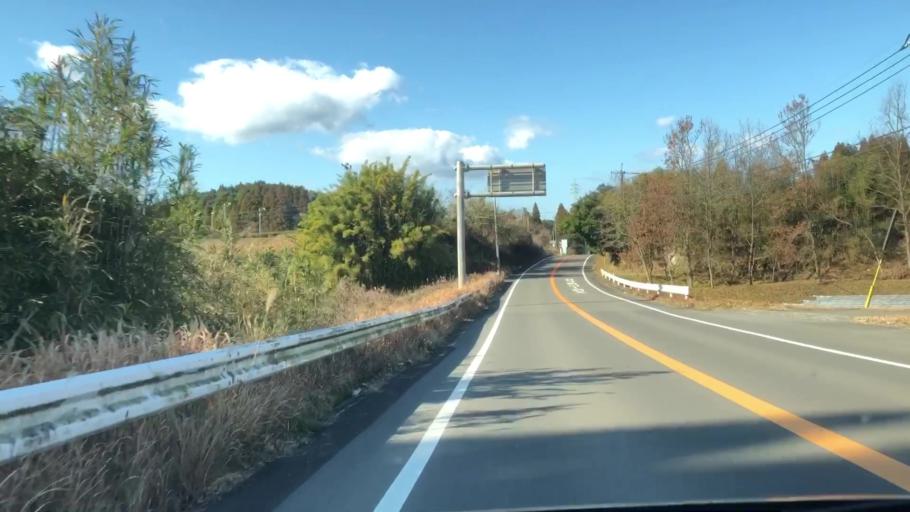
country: JP
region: Kagoshima
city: Satsumasendai
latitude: 31.8430
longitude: 130.4290
